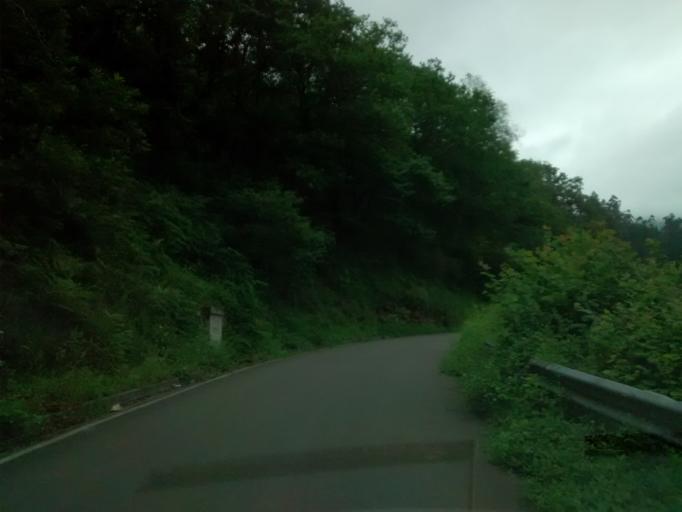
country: ES
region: Asturias
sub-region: Province of Asturias
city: Pilona
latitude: 43.2861
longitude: -5.3526
